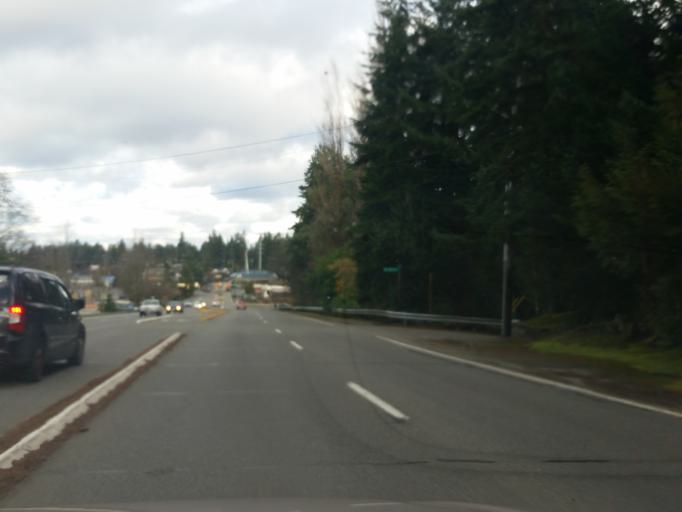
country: US
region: Washington
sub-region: King County
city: Shoreline
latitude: 47.7399
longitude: -122.3497
